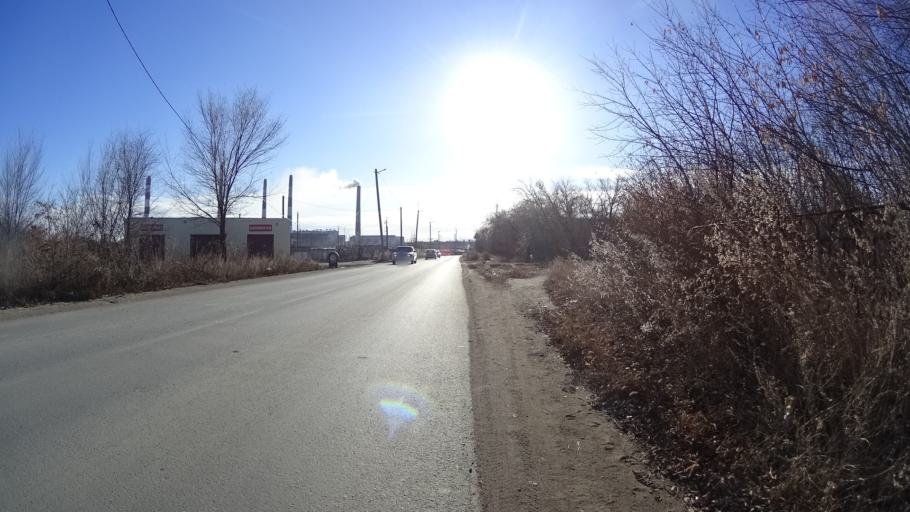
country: RU
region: Chelyabinsk
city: Troitsk
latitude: 54.0459
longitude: 61.6401
